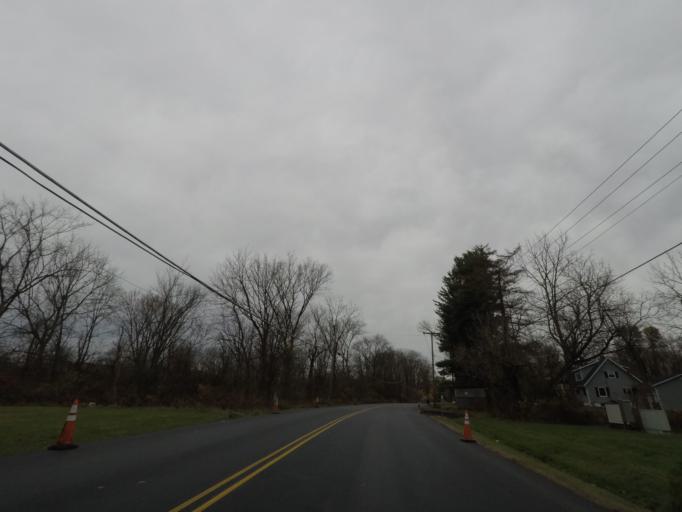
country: US
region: New York
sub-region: Saratoga County
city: Waterford
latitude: 42.8200
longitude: -73.6665
